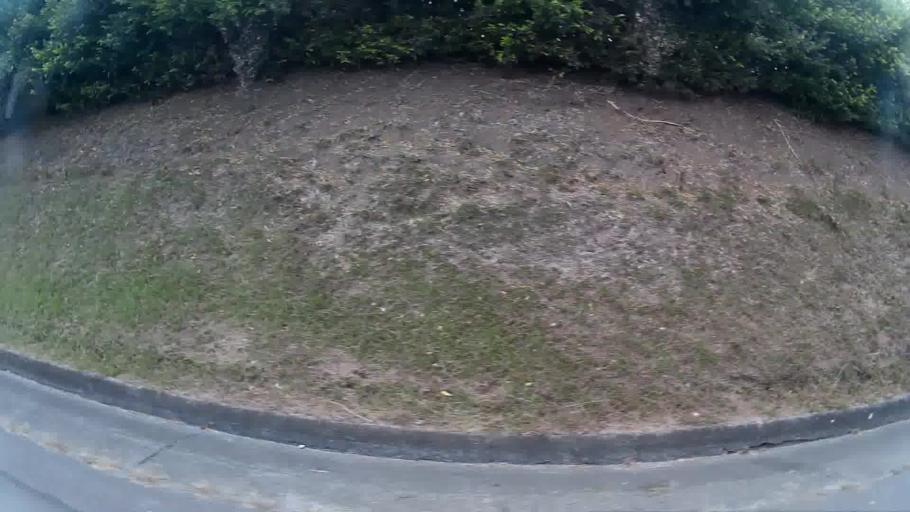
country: CO
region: Risaralda
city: La Virginia
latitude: 4.8388
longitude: -75.8575
